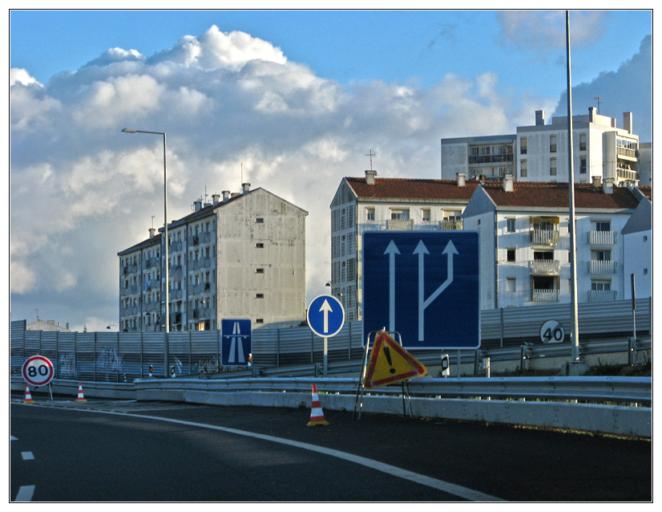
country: PT
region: Lisbon
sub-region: Sintra
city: Cacem
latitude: 38.7893
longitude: -9.3041
